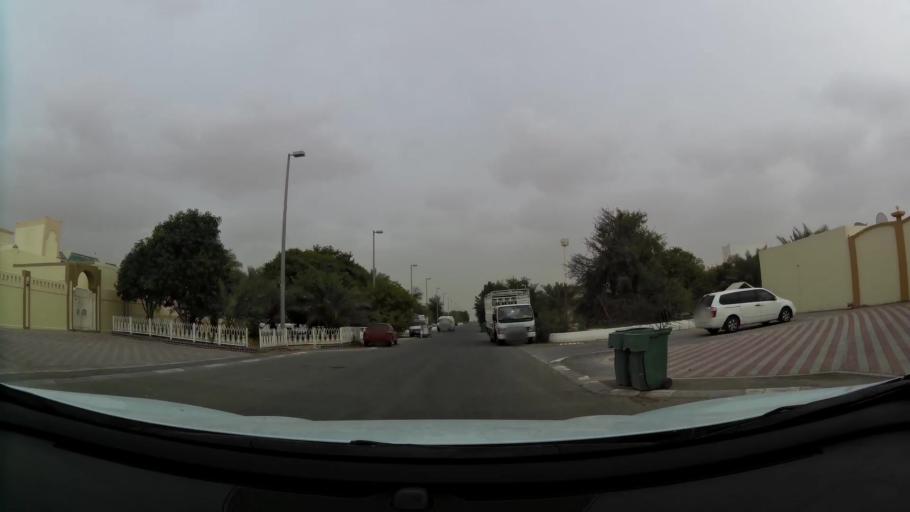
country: AE
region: Abu Dhabi
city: Abu Dhabi
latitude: 24.3744
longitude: 54.6679
